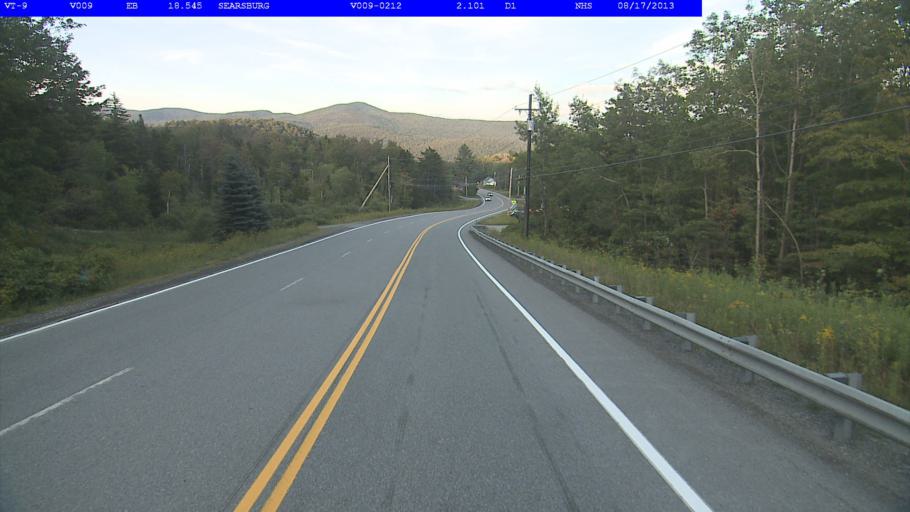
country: US
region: Vermont
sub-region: Windham County
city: Dover
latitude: 42.8947
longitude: -72.9711
